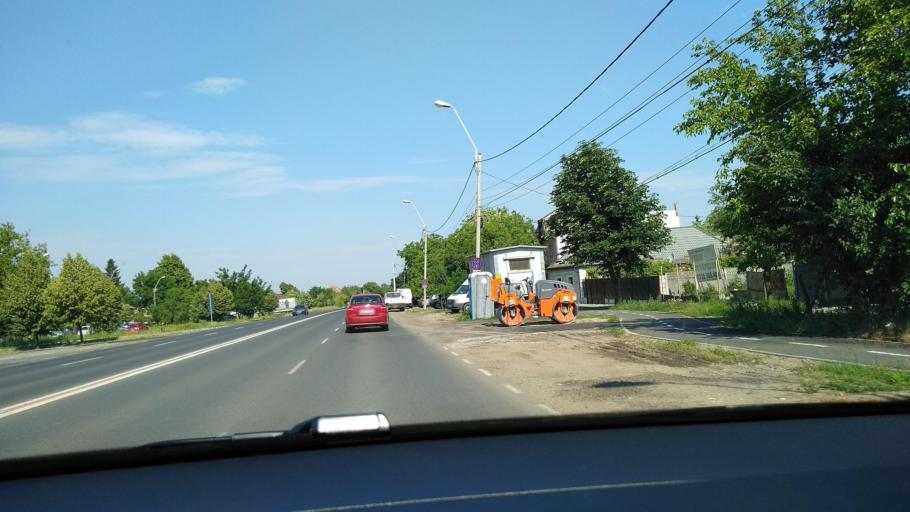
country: RO
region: Timis
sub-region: Comuna Ghiroda
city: Ghiroda
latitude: 45.7275
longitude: 21.2760
